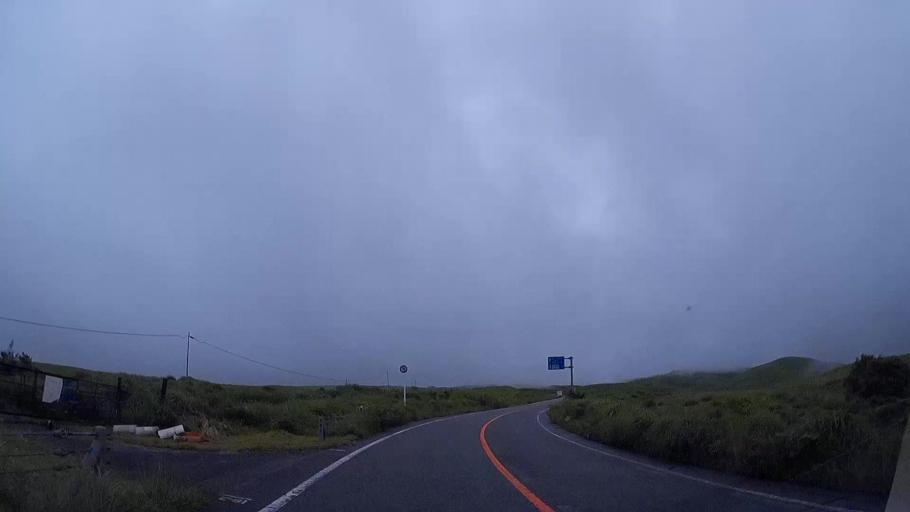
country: JP
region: Kumamoto
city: Aso
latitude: 33.0081
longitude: 131.0692
